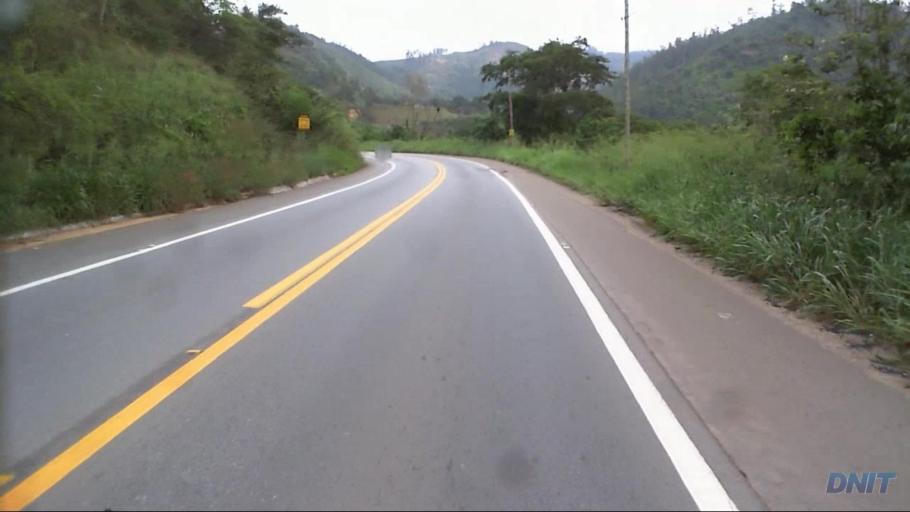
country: BR
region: Minas Gerais
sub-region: Timoteo
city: Timoteo
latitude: -19.5534
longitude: -42.7086
